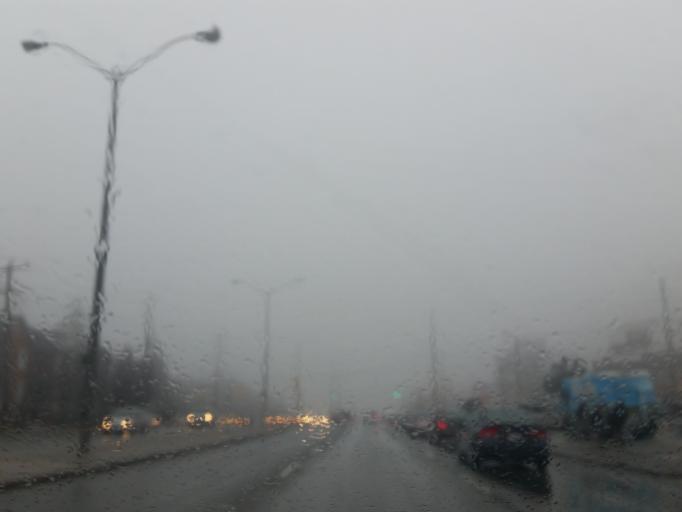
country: CA
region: Ontario
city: Scarborough
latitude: 43.7470
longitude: -79.2086
